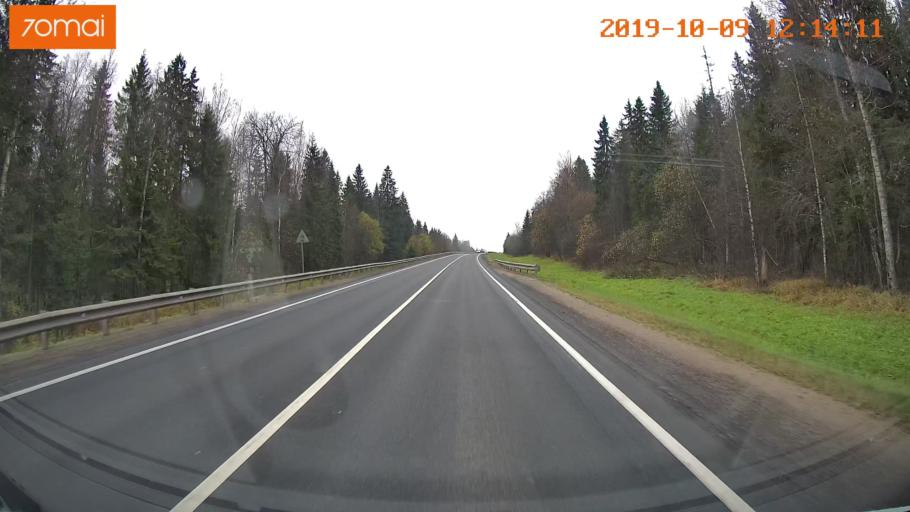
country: RU
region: Jaroslavl
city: Prechistoye
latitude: 58.4994
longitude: 40.3398
